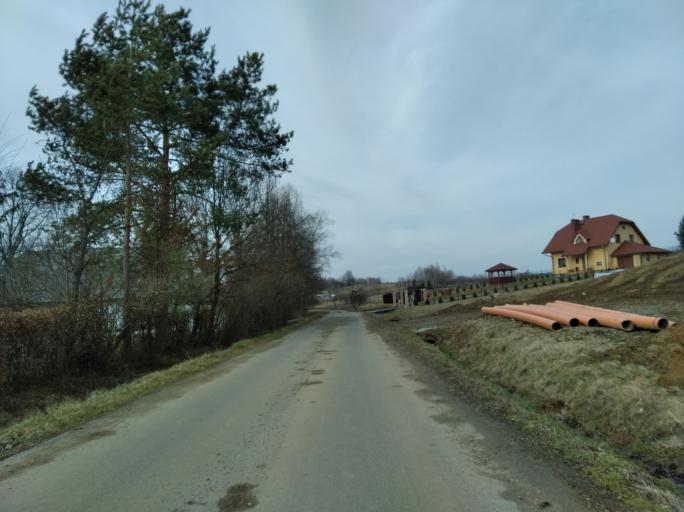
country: PL
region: Subcarpathian Voivodeship
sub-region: Powiat brzozowski
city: Gorki
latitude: 49.6529
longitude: 22.0308
